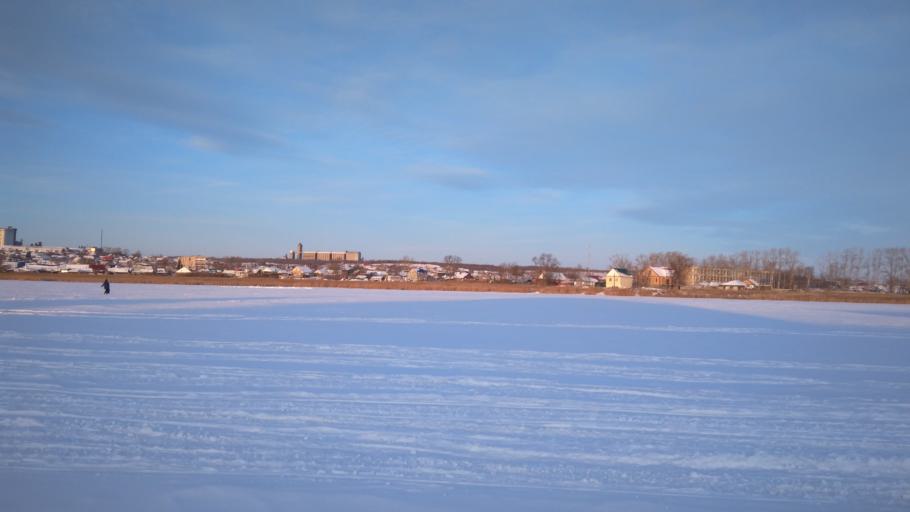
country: RU
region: Chelyabinsk
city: Troitsk
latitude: 54.0882
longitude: 61.5835
